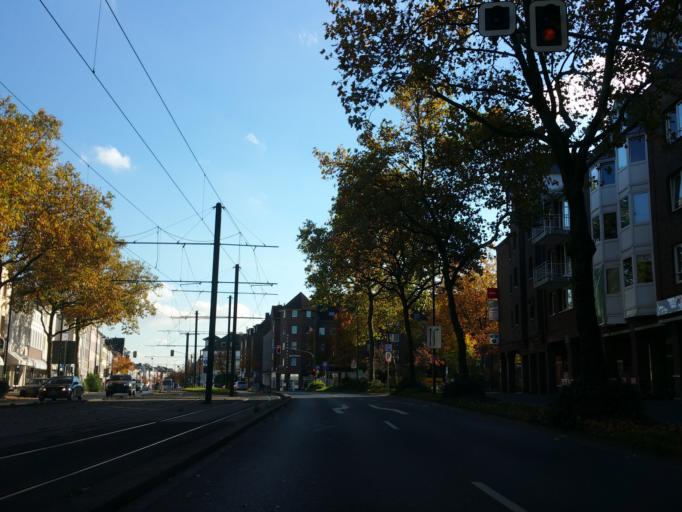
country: DE
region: North Rhine-Westphalia
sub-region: Regierungsbezirk Dusseldorf
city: Dusseldorf
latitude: 51.1916
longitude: 6.8154
